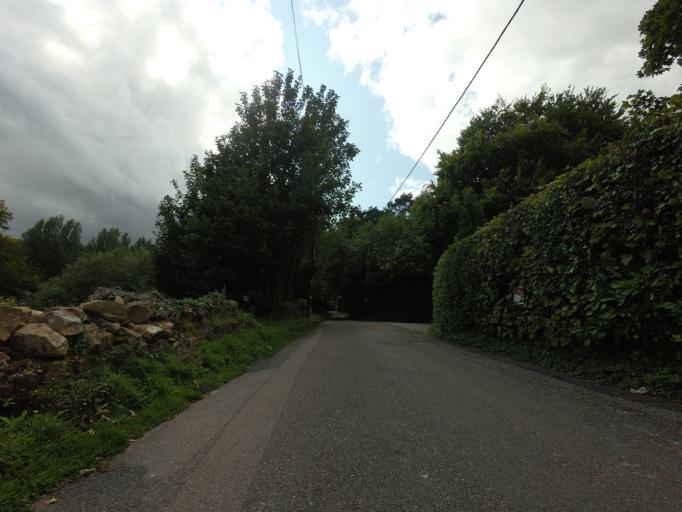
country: GB
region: England
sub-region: Kent
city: Borough Green
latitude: 51.2855
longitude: 0.2735
